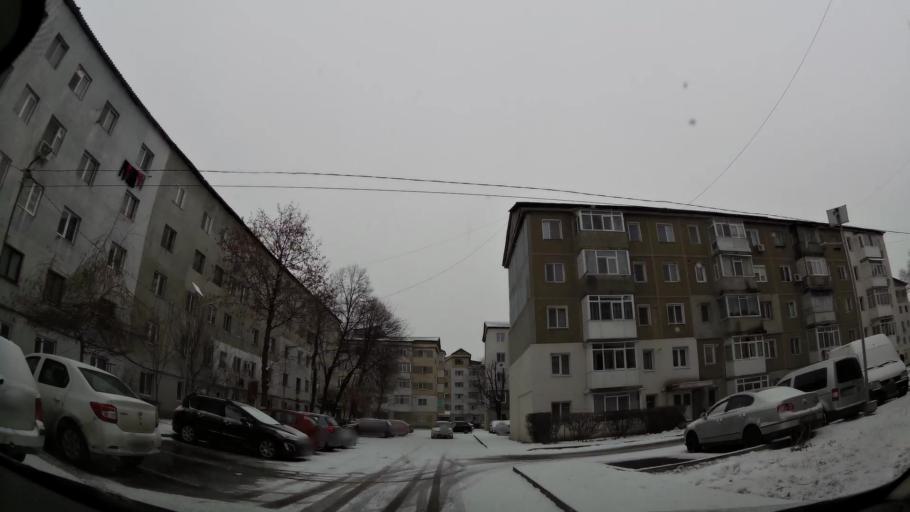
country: RO
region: Dambovita
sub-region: Municipiul Targoviste
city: Targoviste
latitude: 44.9246
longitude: 25.4483
